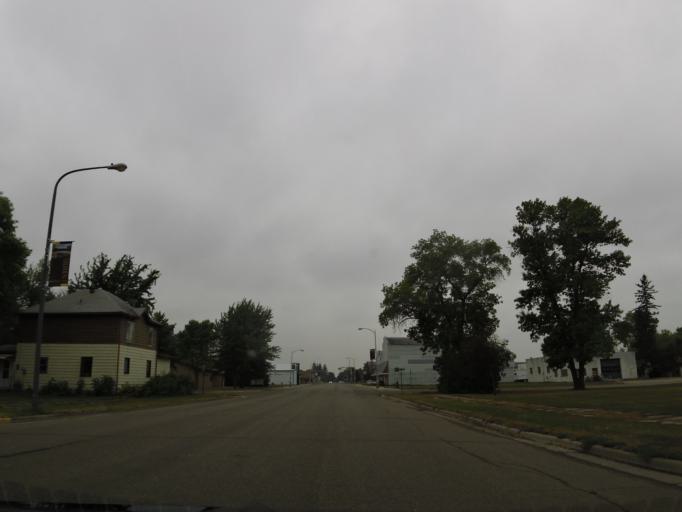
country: US
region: Minnesota
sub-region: Marshall County
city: Warren
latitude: 48.4509
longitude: -96.8703
